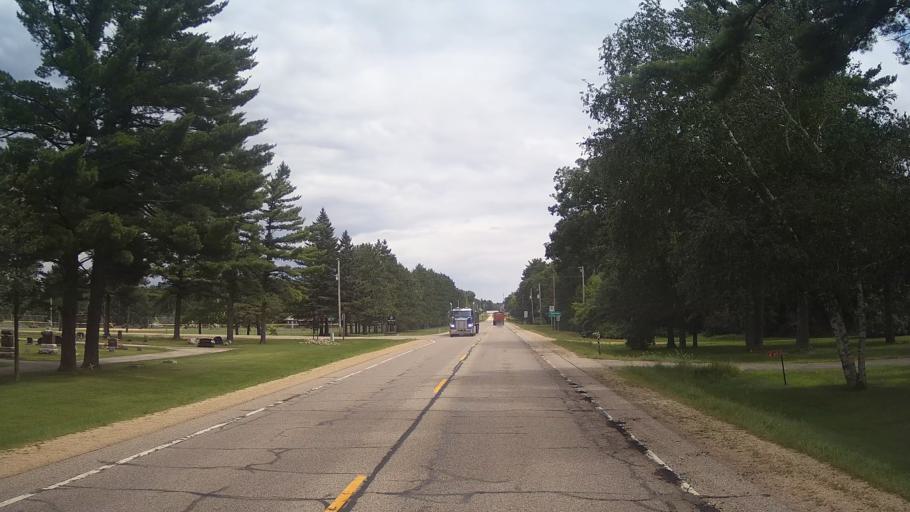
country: US
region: Wisconsin
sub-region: Waushara County
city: Wautoma
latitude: 44.0684
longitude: -89.3087
